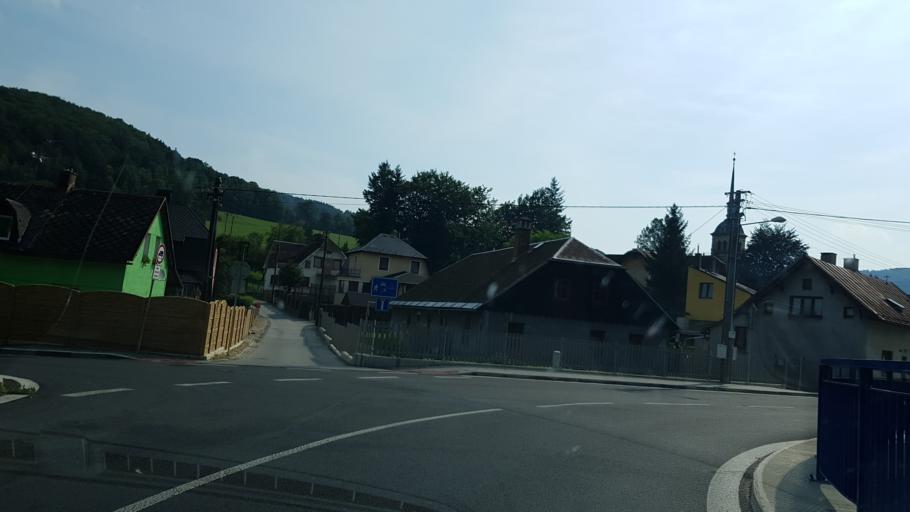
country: CZ
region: Olomoucky
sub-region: Okres Jesenik
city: Jesenik
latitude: 50.2196
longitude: 17.2089
